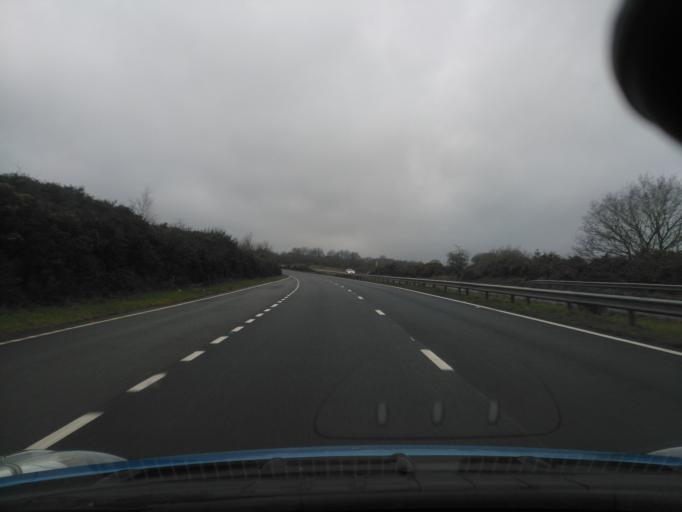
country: GB
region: England
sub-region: Surrey
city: Elstead
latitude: 51.1474
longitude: -0.7031
